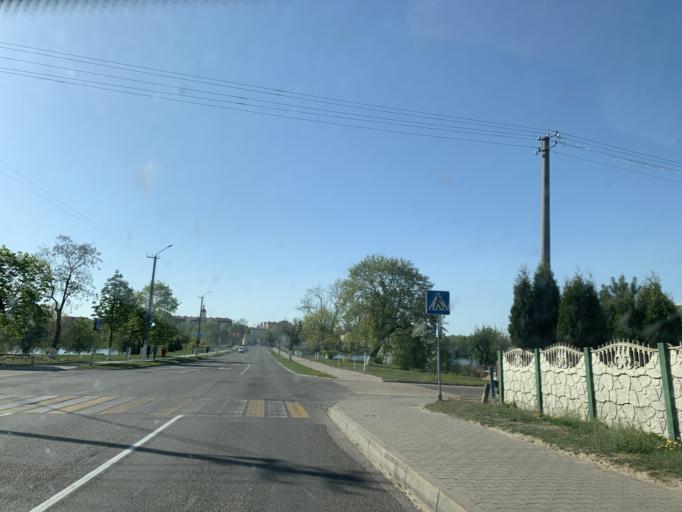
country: BY
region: Minsk
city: Nyasvizh
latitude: 53.2161
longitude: 26.6894
